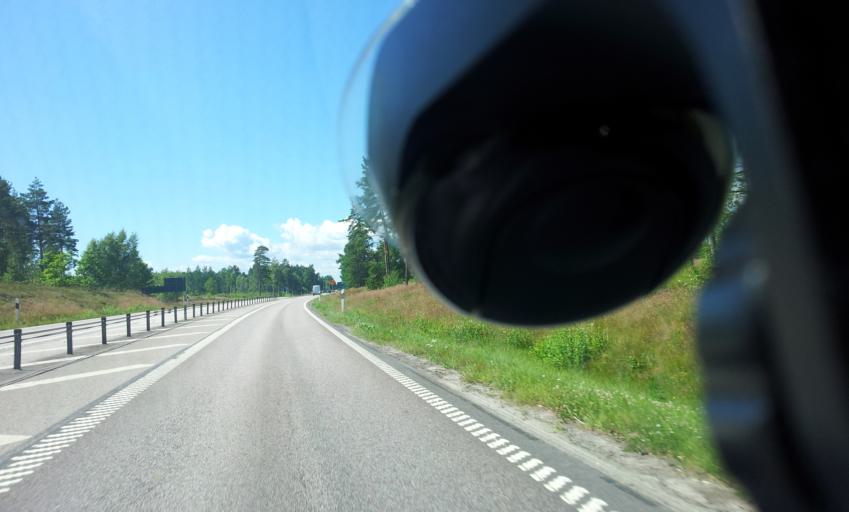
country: SE
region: Kalmar
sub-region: Monsteras Kommun
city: Moensteras
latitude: 57.0774
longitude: 16.4810
